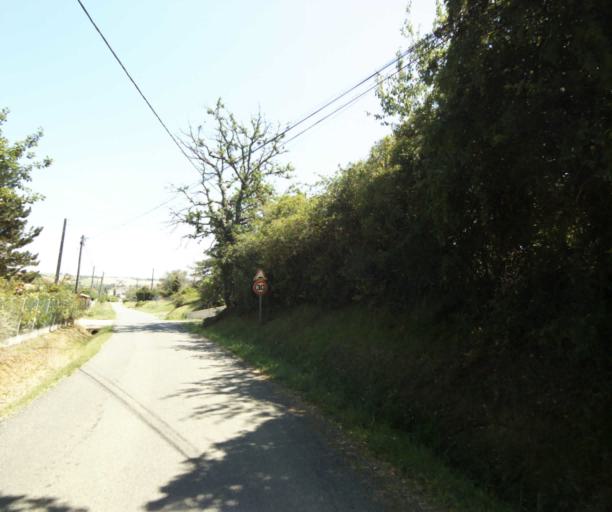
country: FR
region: Midi-Pyrenees
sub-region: Departement de l'Ariege
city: Lezat-sur-Leze
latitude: 43.2772
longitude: 1.3368
